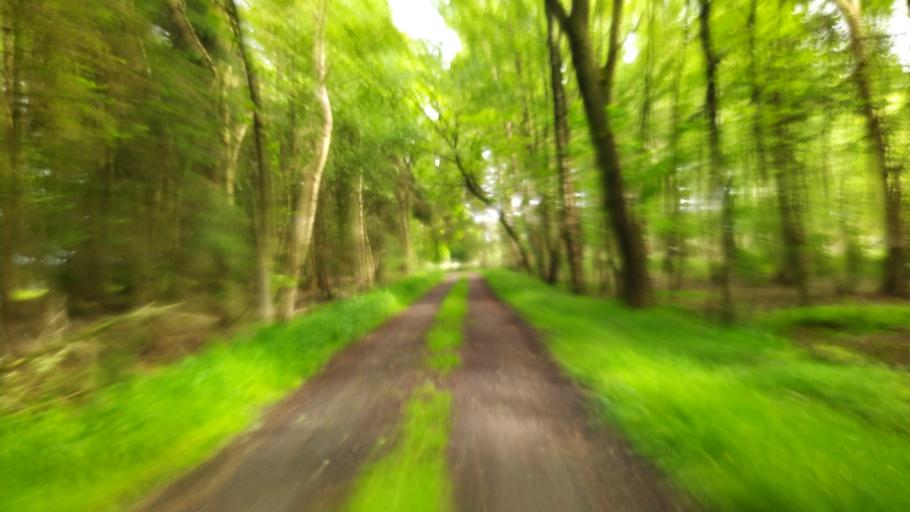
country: DE
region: Lower Saxony
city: Brest
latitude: 53.4230
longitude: 9.3569
